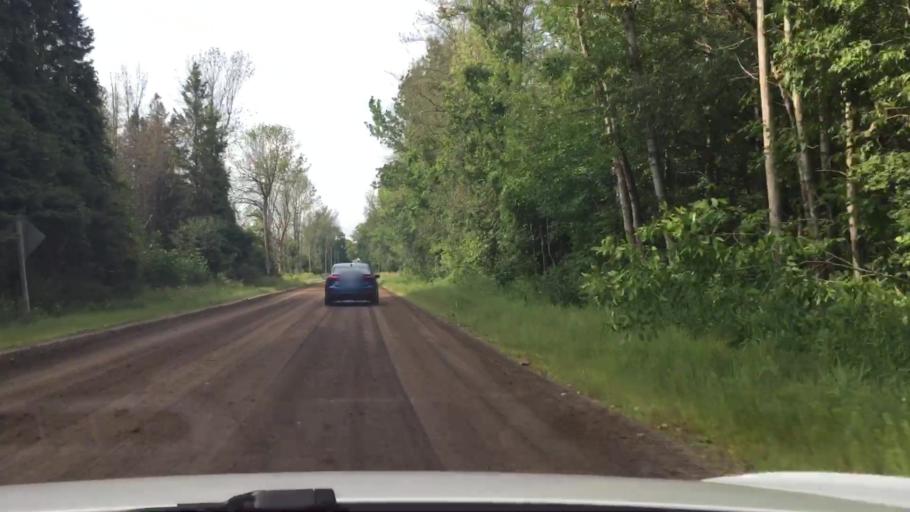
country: CA
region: Ontario
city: Oshawa
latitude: 43.9266
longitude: -78.7412
